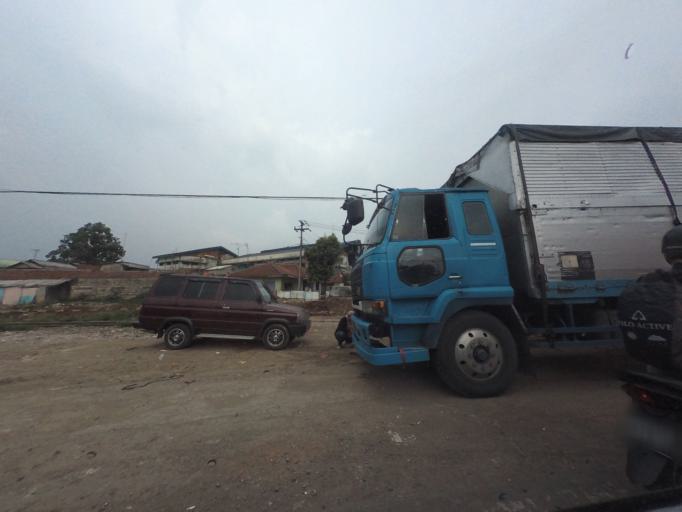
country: ID
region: West Java
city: Cicurug
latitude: -6.7640
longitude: 106.8027
